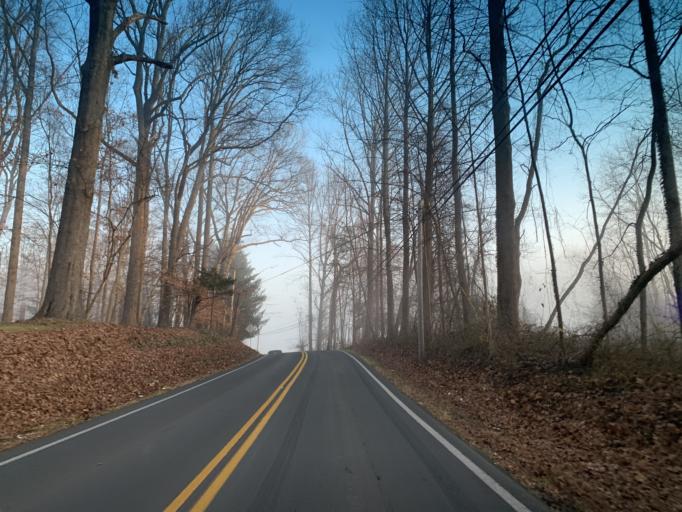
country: US
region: Maryland
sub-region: Harford County
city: Pleasant Hills
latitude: 39.4920
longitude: -76.3740
